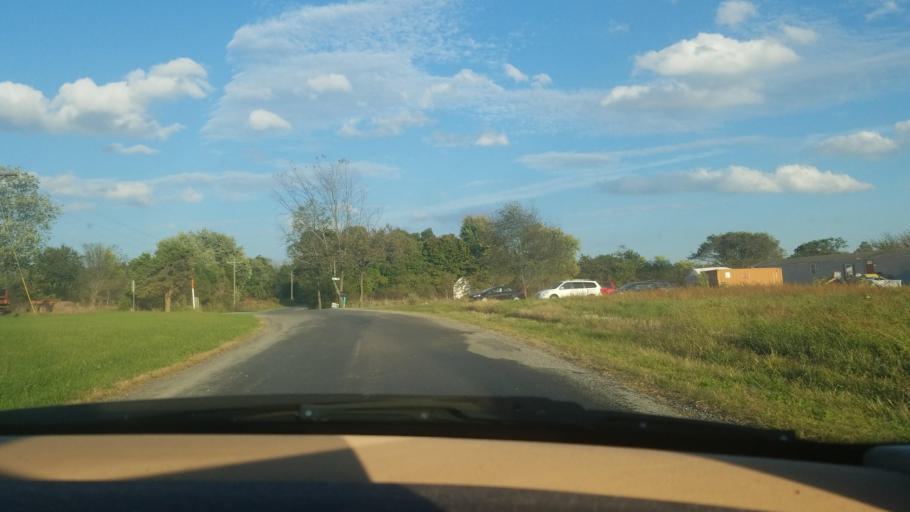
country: US
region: Illinois
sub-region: Saline County
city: Carrier Mills
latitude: 37.7713
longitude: -88.7537
